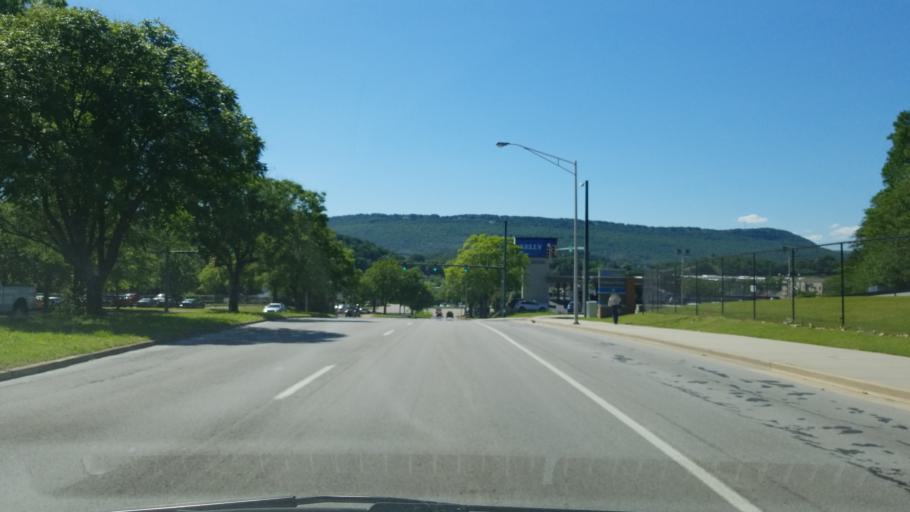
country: US
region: Tennessee
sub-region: Hamilton County
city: Chattanooga
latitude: 35.0485
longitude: -85.3188
